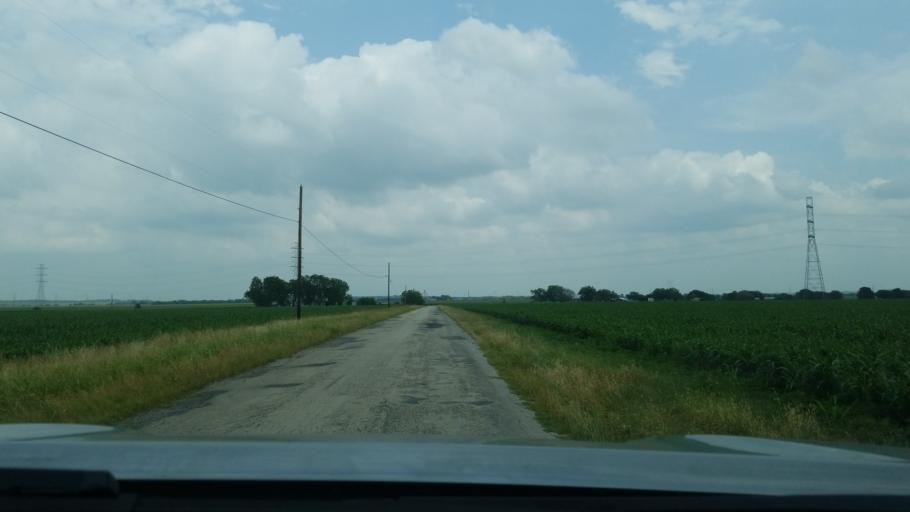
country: US
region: Texas
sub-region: Guadalupe County
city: Lake Dunlap
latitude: 29.6775
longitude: -98.0191
